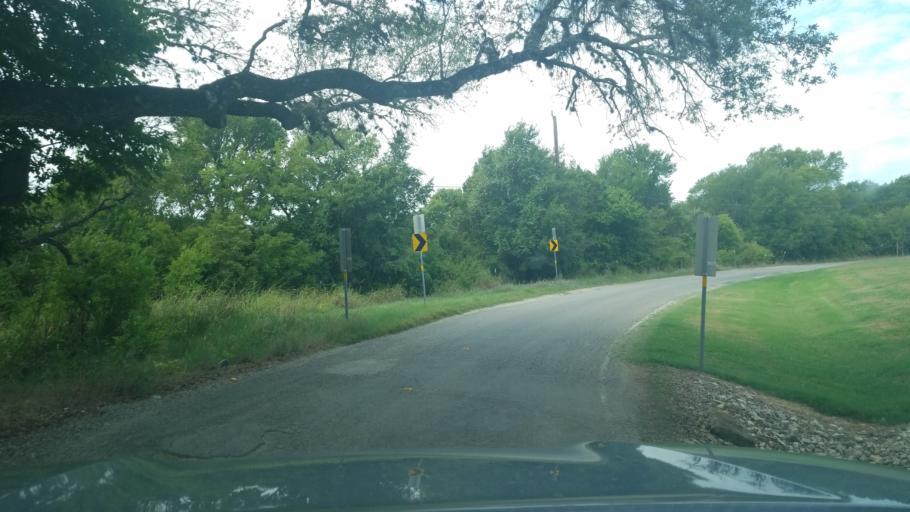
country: US
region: Texas
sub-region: Comal County
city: Bulverde
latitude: 29.7598
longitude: -98.4089
